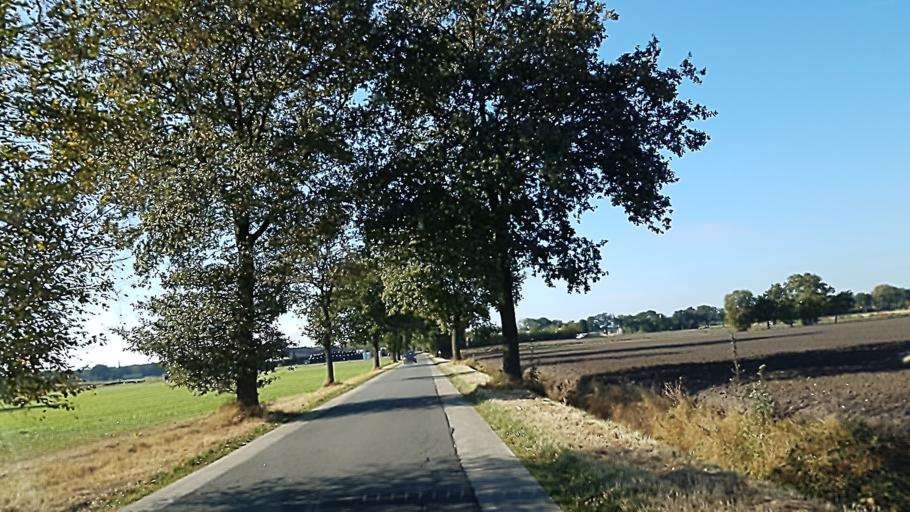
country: BE
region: Flanders
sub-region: Provincie Antwerpen
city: Essen
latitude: 51.4350
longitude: 4.4040
